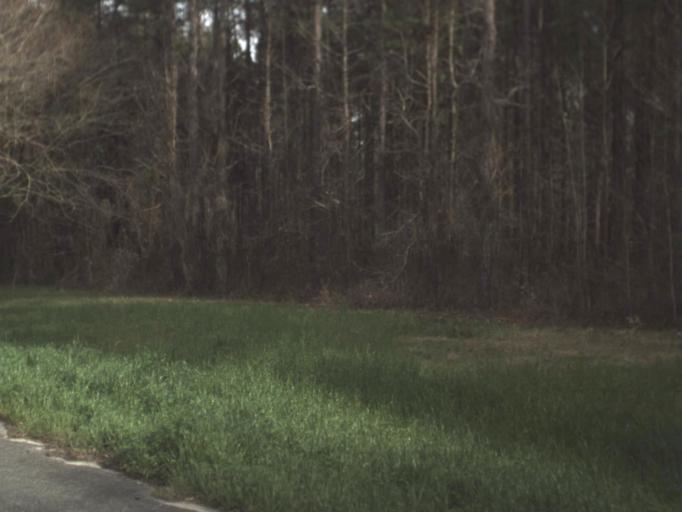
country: US
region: Florida
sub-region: Jefferson County
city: Monticello
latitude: 30.5384
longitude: -83.9248
